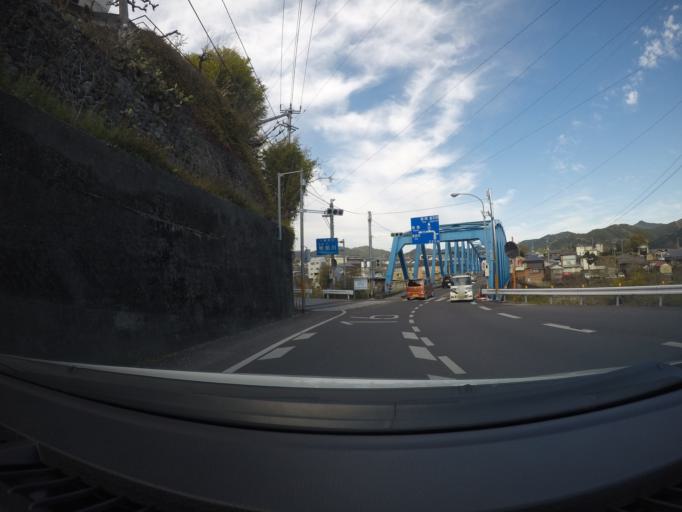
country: JP
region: Kochi
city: Kochi-shi
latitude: 33.6151
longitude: 133.7133
